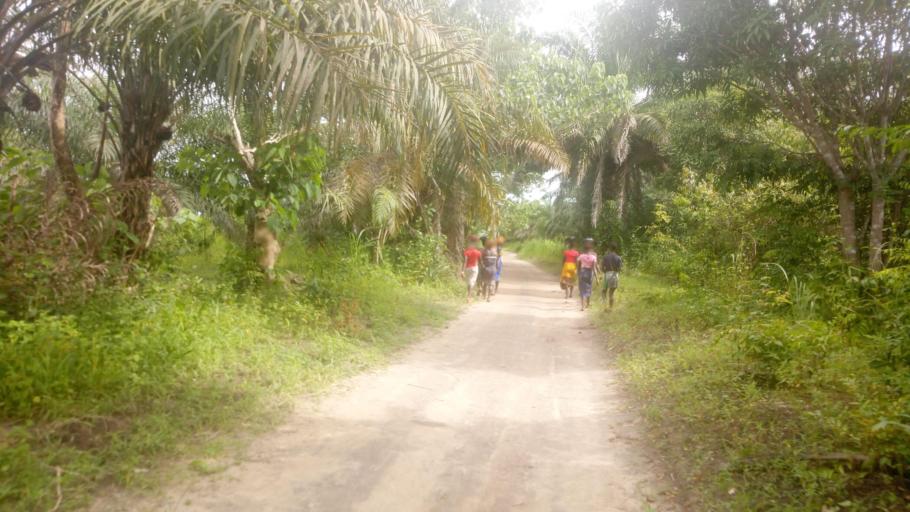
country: SL
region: Northern Province
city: Magburaka
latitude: 8.6752
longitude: -12.0320
